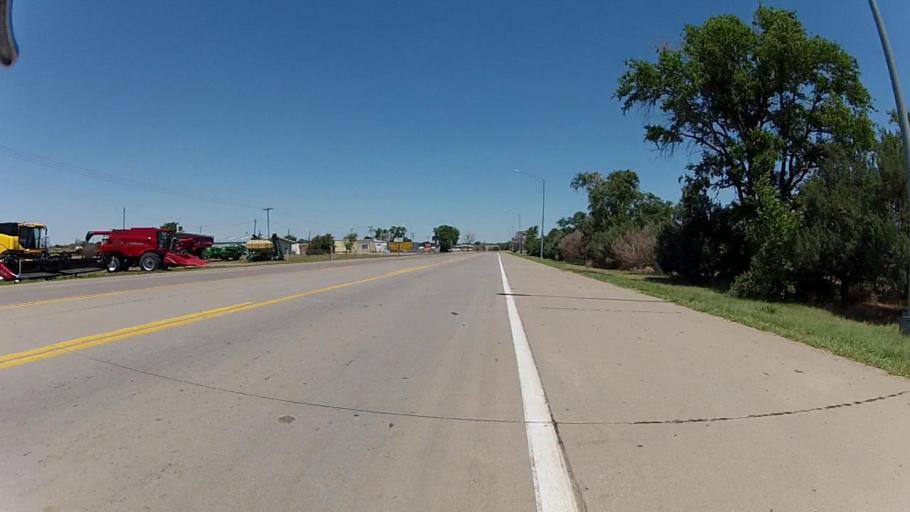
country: US
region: Kansas
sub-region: Ford County
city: Dodge City
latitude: 37.7268
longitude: -100.0170
